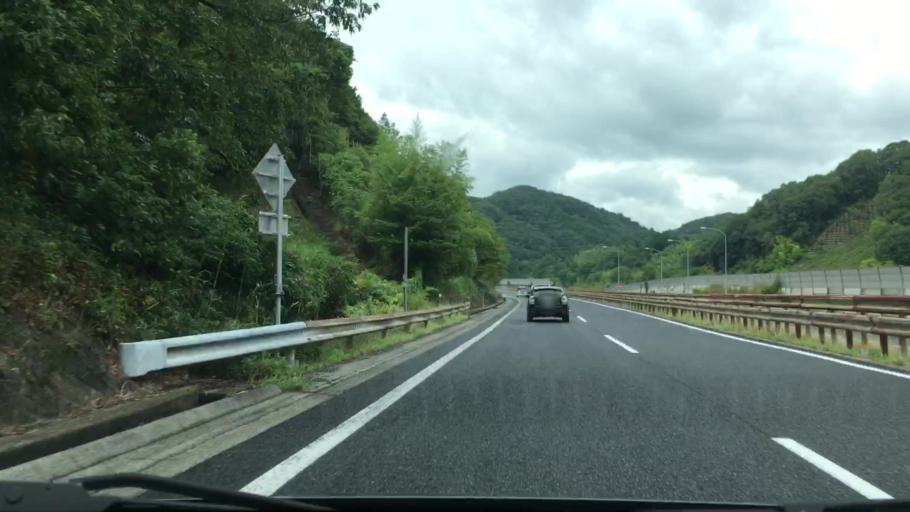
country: JP
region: Okayama
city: Tsuyama
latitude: 35.0156
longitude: 134.2529
